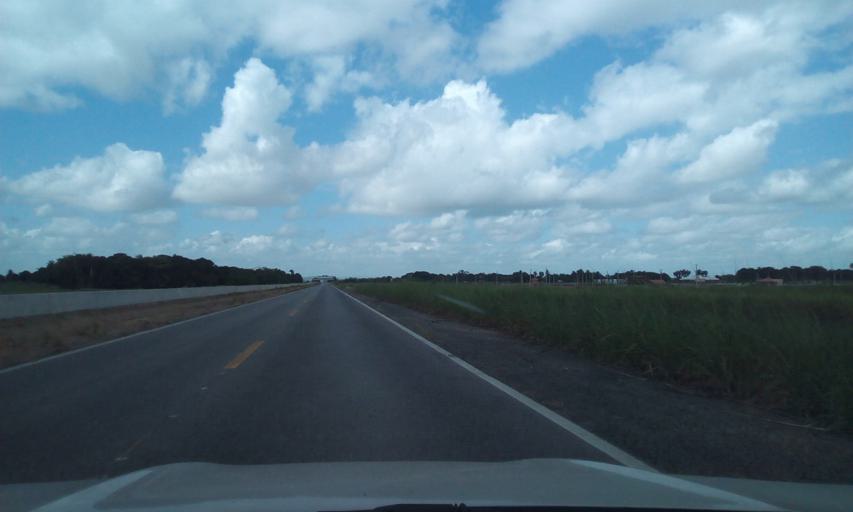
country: BR
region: Alagoas
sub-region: Pilar
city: Pilar
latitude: -9.5776
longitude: -35.9724
